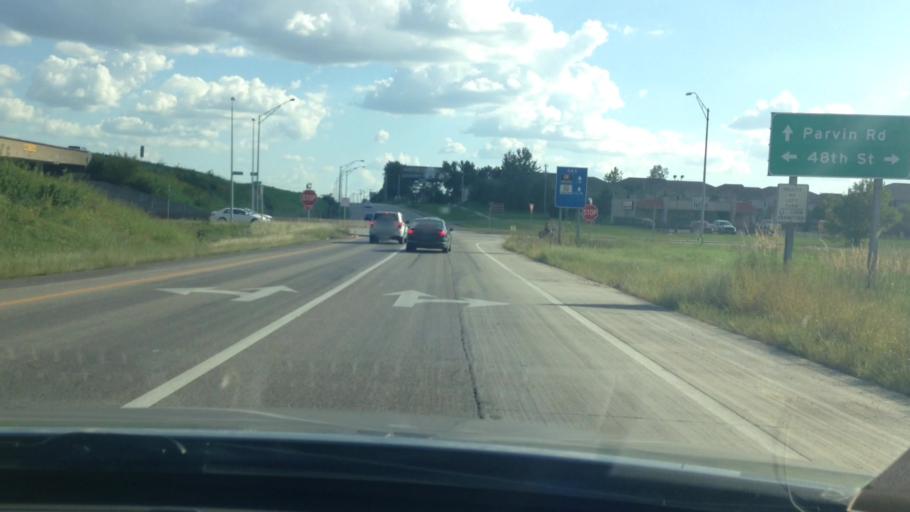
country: US
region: Missouri
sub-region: Clay County
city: Claycomo
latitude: 39.1814
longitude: -94.4935
